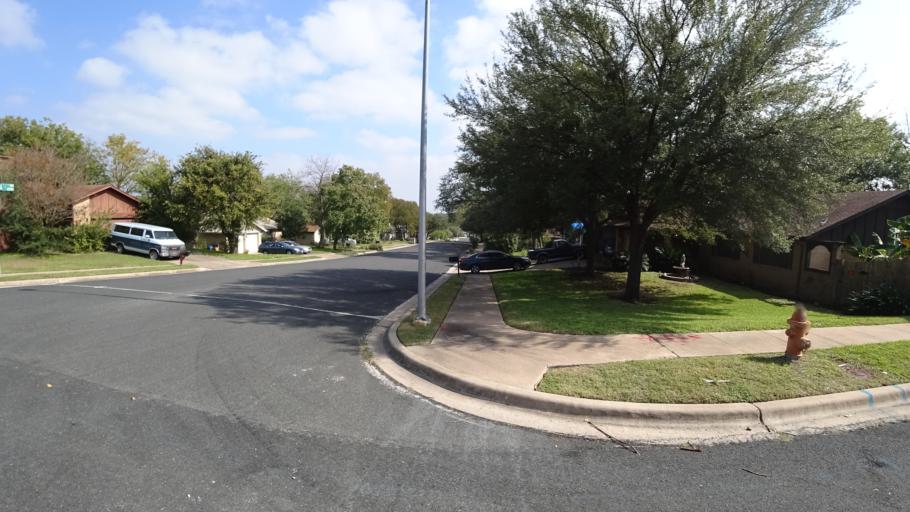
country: US
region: Texas
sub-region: Travis County
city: Shady Hollow
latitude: 30.2049
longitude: -97.8198
